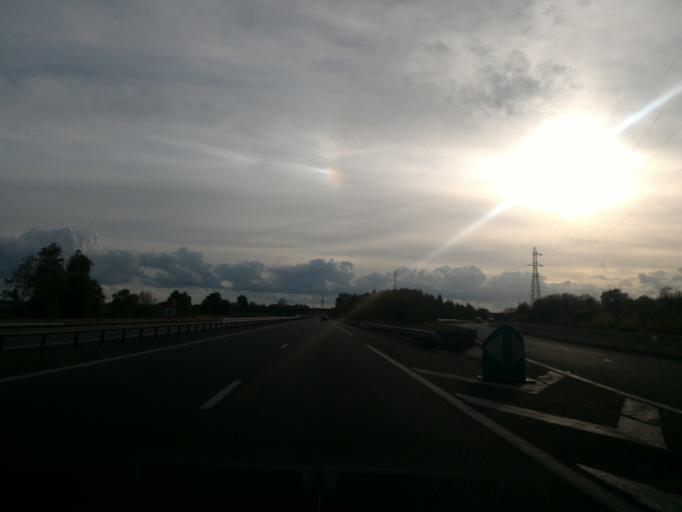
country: FR
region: Alsace
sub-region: Departement du Haut-Rhin
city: Burnhaupt-le-Bas
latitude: 47.7273
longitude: 7.1720
